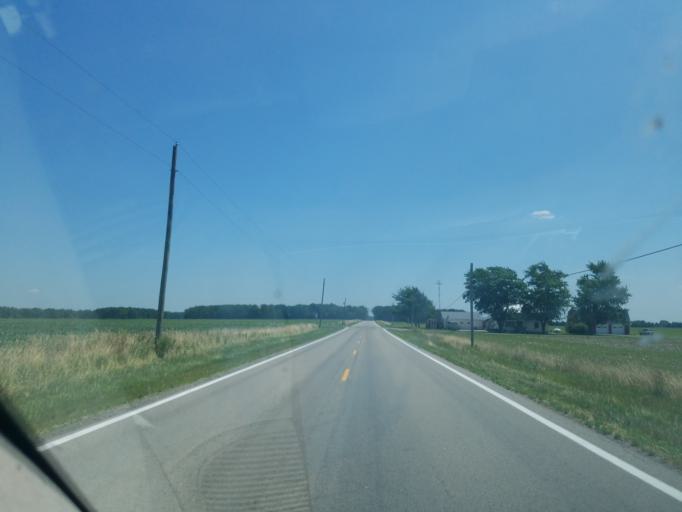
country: US
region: Ohio
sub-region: Allen County
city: Spencerville
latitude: 40.7427
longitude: -84.4462
